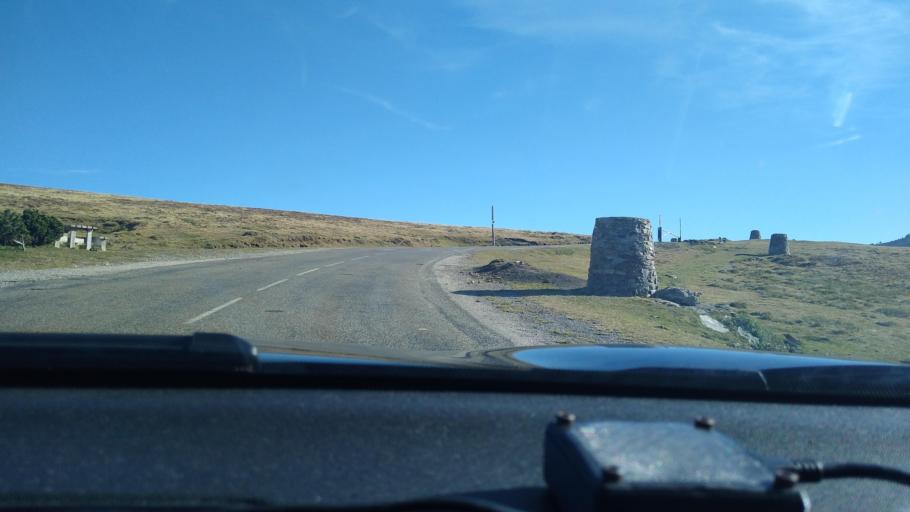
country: FR
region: Midi-Pyrenees
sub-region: Departement de l'Ariege
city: Ax-les-Thermes
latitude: 42.7328
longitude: 1.9877
